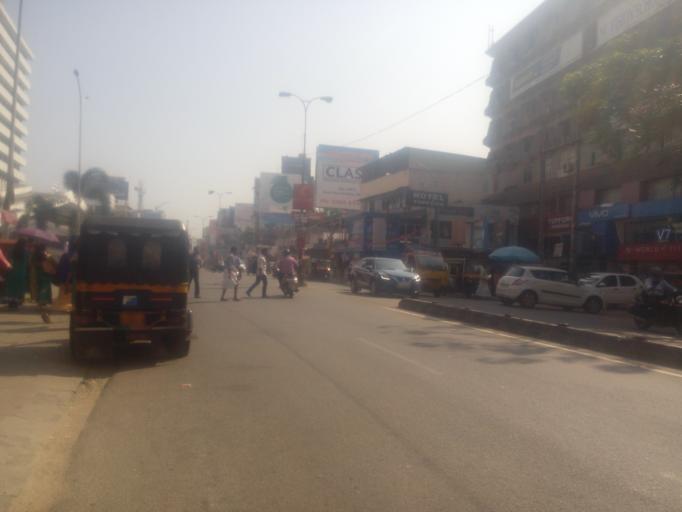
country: IN
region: Kerala
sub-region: Kozhikode
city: Kozhikode
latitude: 11.2591
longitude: 75.7816
